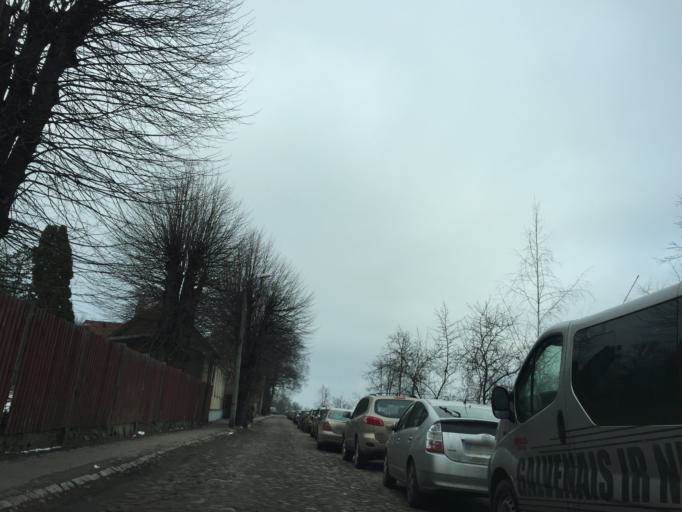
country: LV
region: Riga
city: Riga
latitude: 56.9512
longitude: 24.0867
